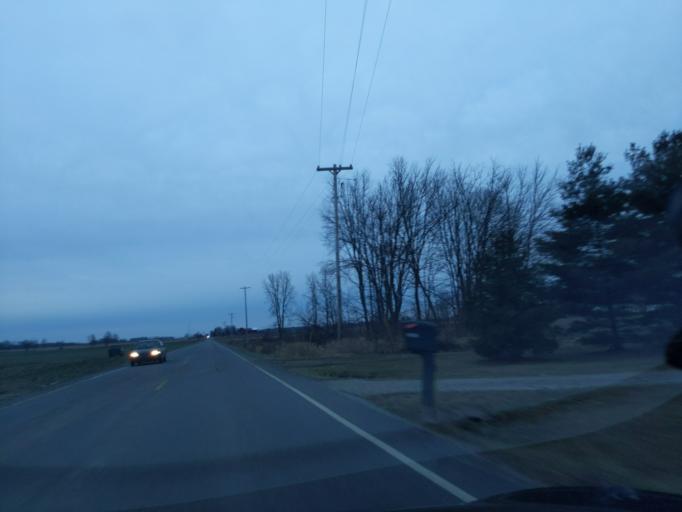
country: US
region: Michigan
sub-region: Ionia County
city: Portland
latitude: 42.8952
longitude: -84.9561
